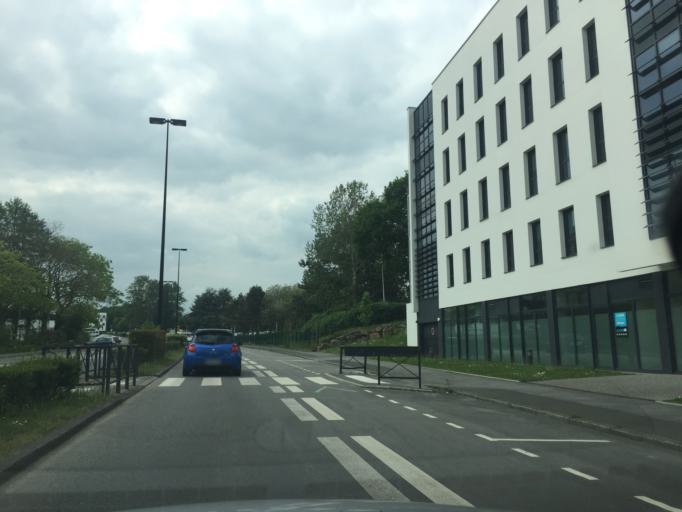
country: FR
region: Pays de la Loire
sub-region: Departement de la Loire-Atlantique
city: La Chapelle-sur-Erdre
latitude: 47.2633
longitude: -1.5686
